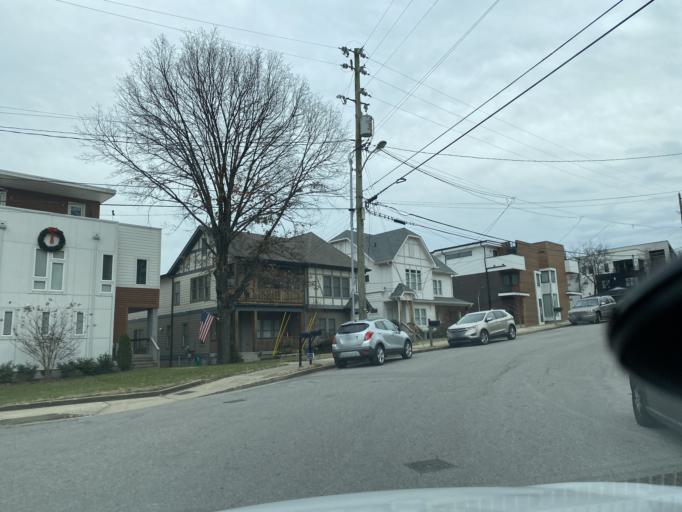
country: US
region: Tennessee
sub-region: Davidson County
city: Nashville
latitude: 36.1459
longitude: -86.7805
